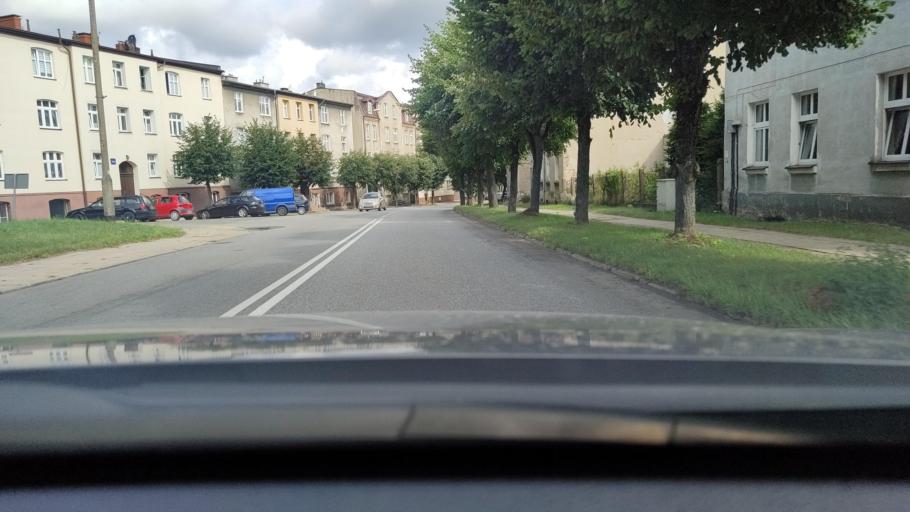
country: PL
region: Pomeranian Voivodeship
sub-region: Powiat wejherowski
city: Wejherowo
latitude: 54.5976
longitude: 18.2322
